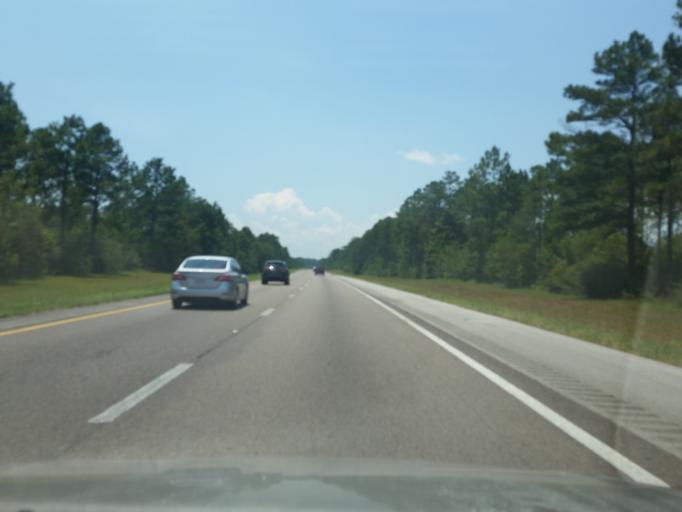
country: US
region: Florida
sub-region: Escambia County
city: Cantonment
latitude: 30.5787
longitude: -87.4423
